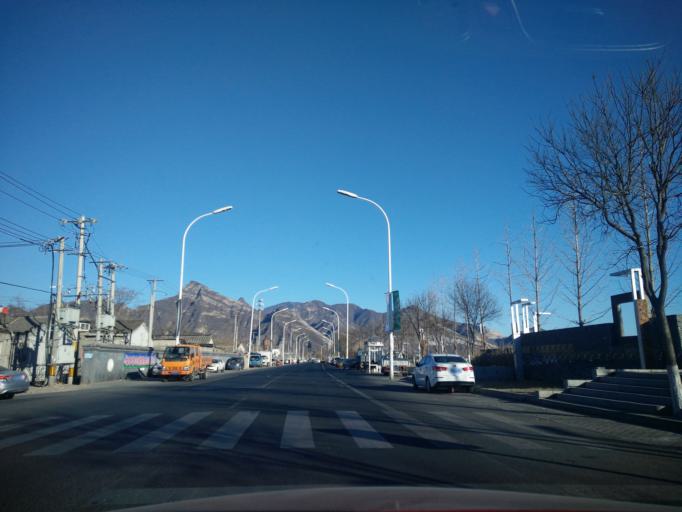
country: CN
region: Beijing
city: Junzhuang
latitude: 39.9823
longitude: 116.0819
